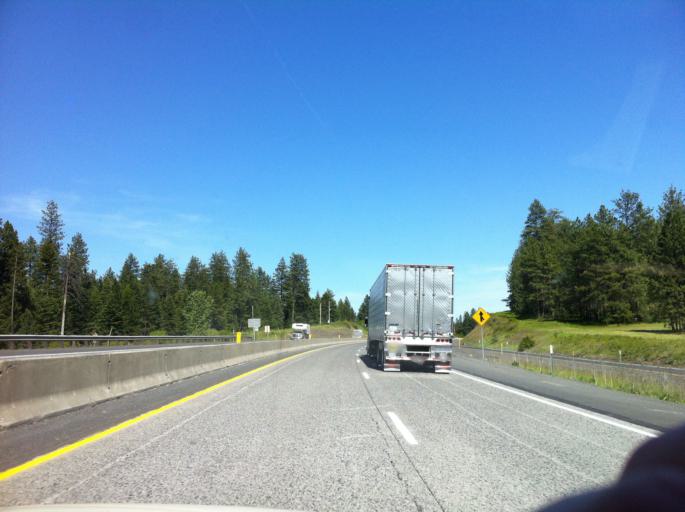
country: US
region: Oregon
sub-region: Umatilla County
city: Mission
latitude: 45.5994
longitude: -118.5081
